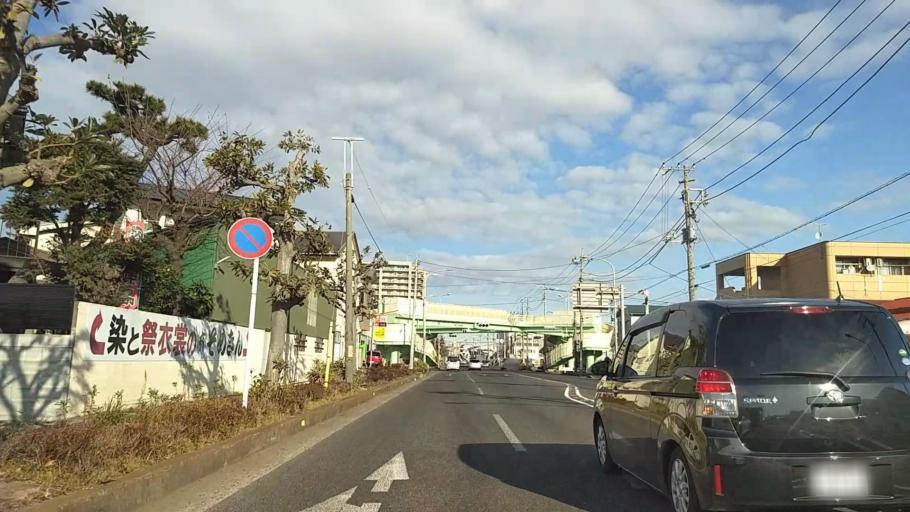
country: JP
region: Kanagawa
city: Hiratsuka
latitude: 35.3232
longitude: 139.3607
